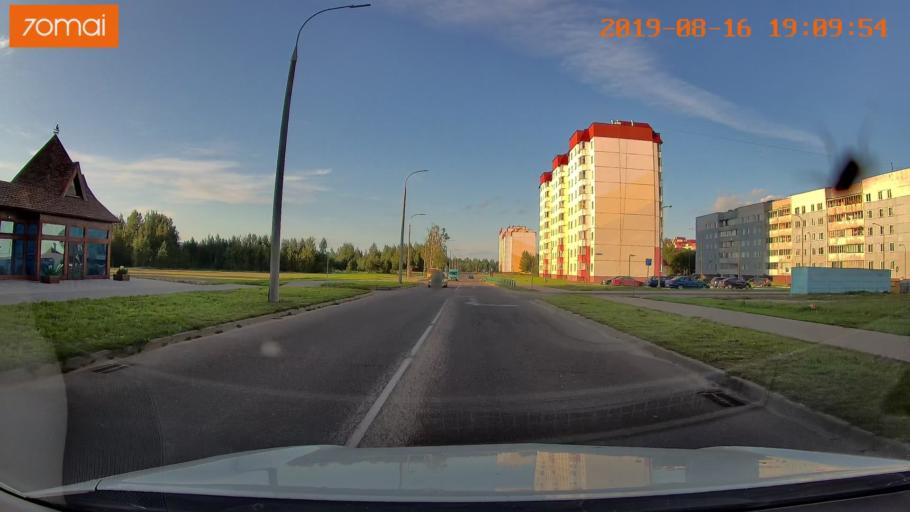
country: BY
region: Mogilev
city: Asipovichy
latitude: 53.3210
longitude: 28.6370
